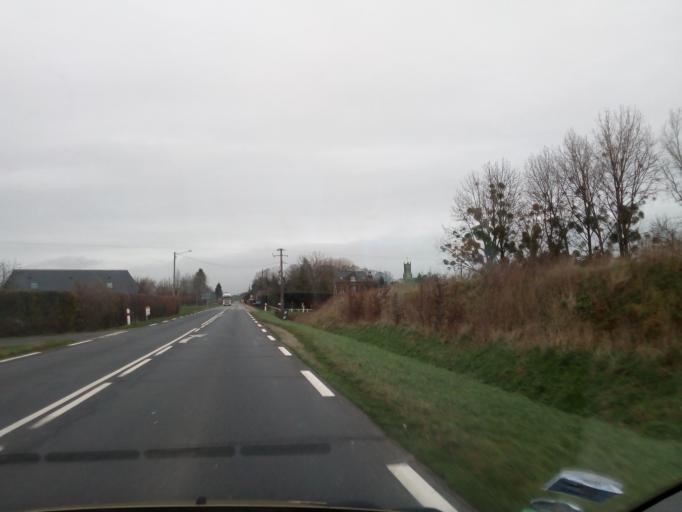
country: FR
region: Haute-Normandie
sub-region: Departement de l'Eure
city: Hauville
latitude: 49.3993
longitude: 0.7977
